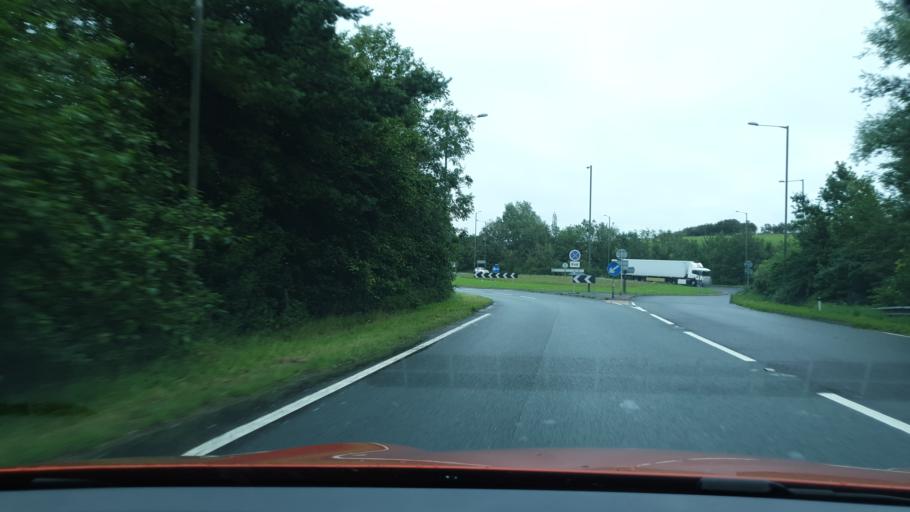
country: GB
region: England
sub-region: Cumbria
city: Dalton in Furness
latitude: 54.1655
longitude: -3.1651
